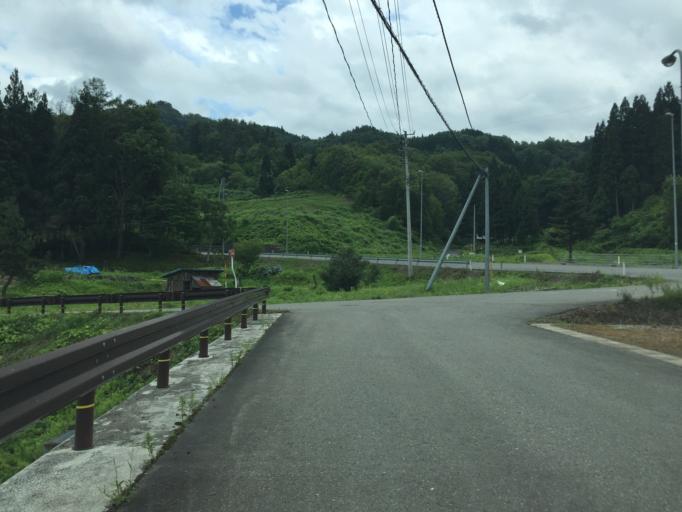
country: JP
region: Yamagata
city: Yonezawa
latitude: 37.8510
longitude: 140.0962
